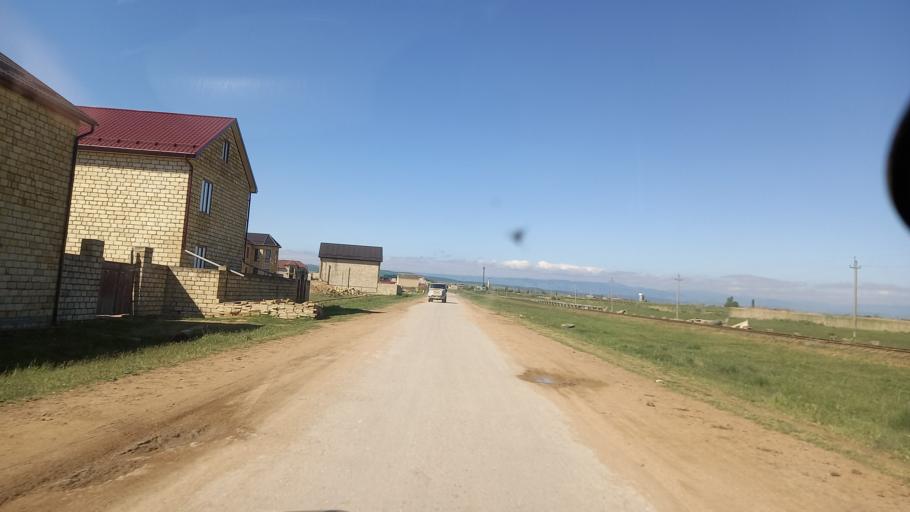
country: RU
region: Dagestan
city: Dagestanskiye Ogni
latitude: 42.1292
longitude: 48.2235
